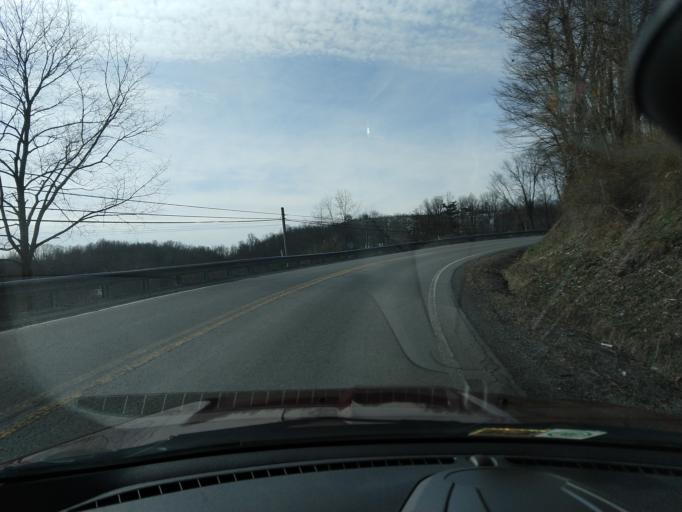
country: US
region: West Virginia
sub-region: Pocahontas County
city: Marlinton
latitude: 38.1200
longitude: -80.2408
